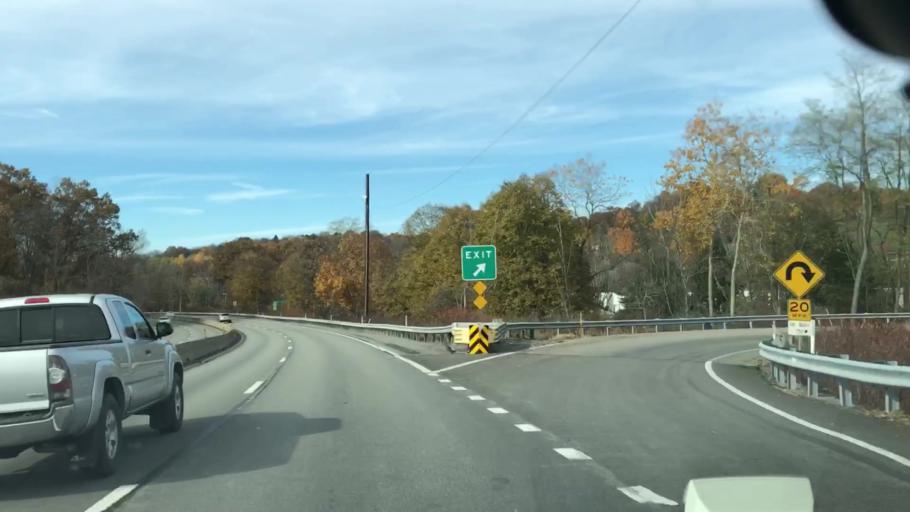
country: US
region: Pennsylvania
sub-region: Allegheny County
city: Franklin Park
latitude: 40.5840
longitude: -80.0313
